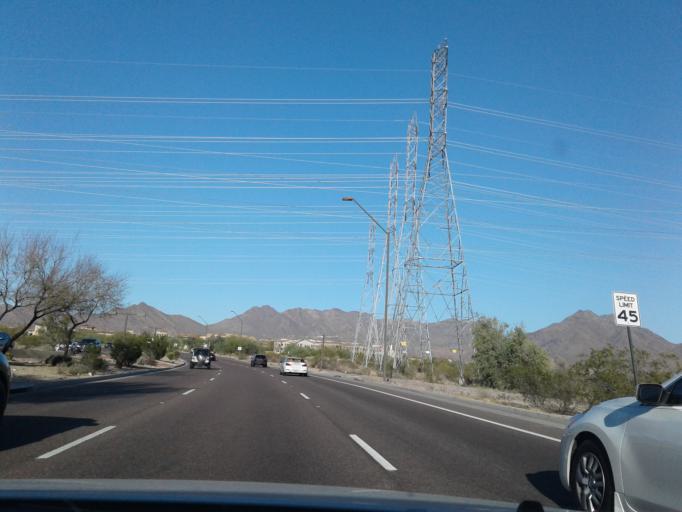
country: US
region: Arizona
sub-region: Maricopa County
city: Paradise Valley
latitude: 33.6483
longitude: -111.8901
